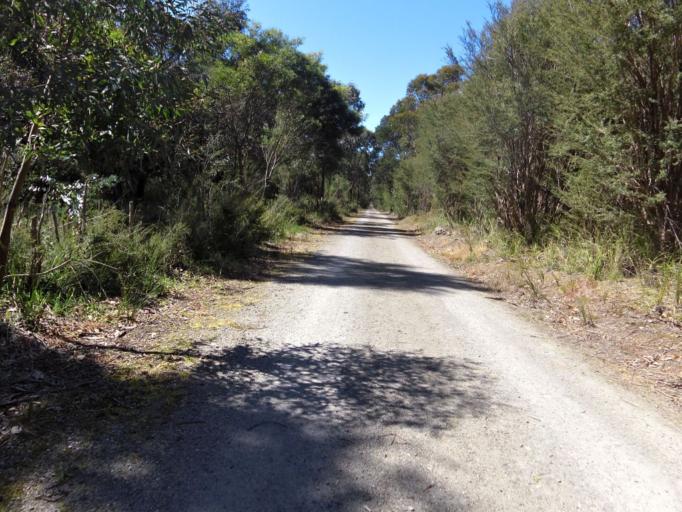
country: AU
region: Victoria
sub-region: Latrobe
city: Moe
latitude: -38.1725
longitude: 146.2878
